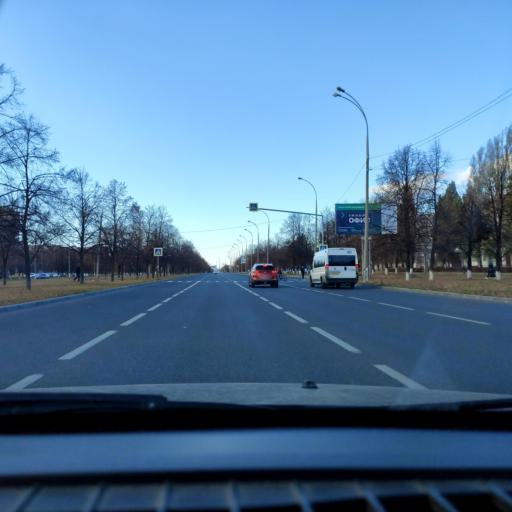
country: RU
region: Samara
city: Tol'yatti
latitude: 53.5179
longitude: 49.3033
